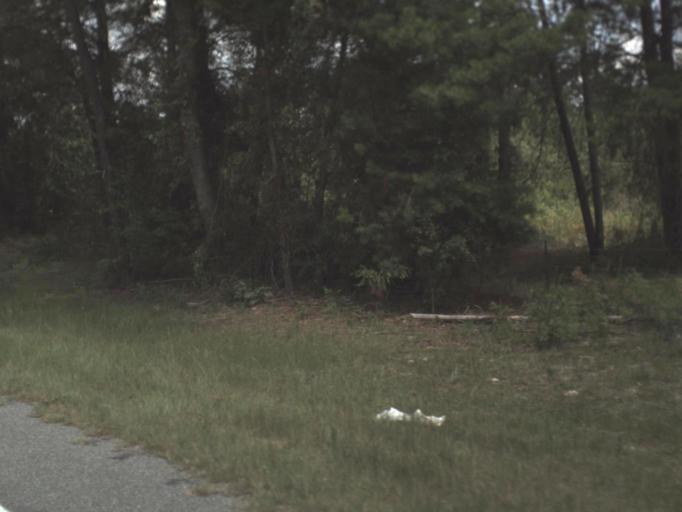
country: US
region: Florida
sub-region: Madison County
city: Madison
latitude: 30.4869
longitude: -83.1821
